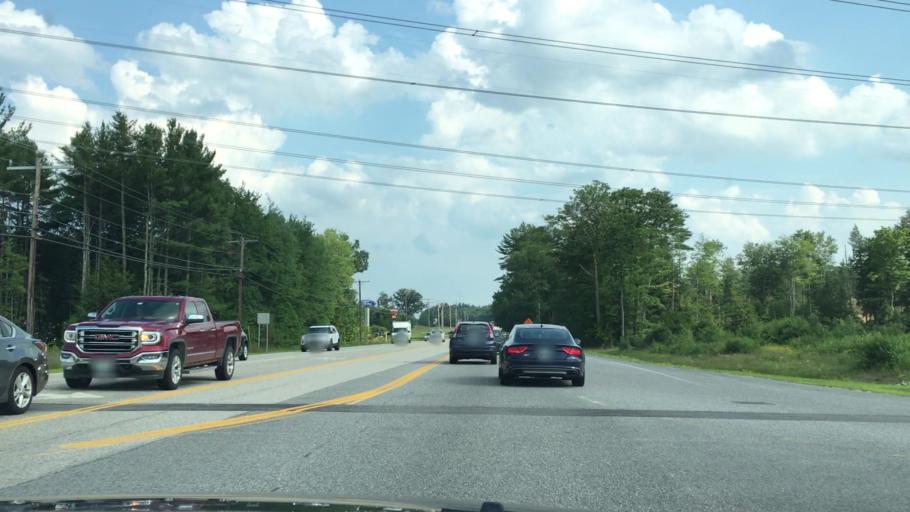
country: US
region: New Hampshire
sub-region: Strafford County
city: Rochester
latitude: 43.3315
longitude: -71.0067
